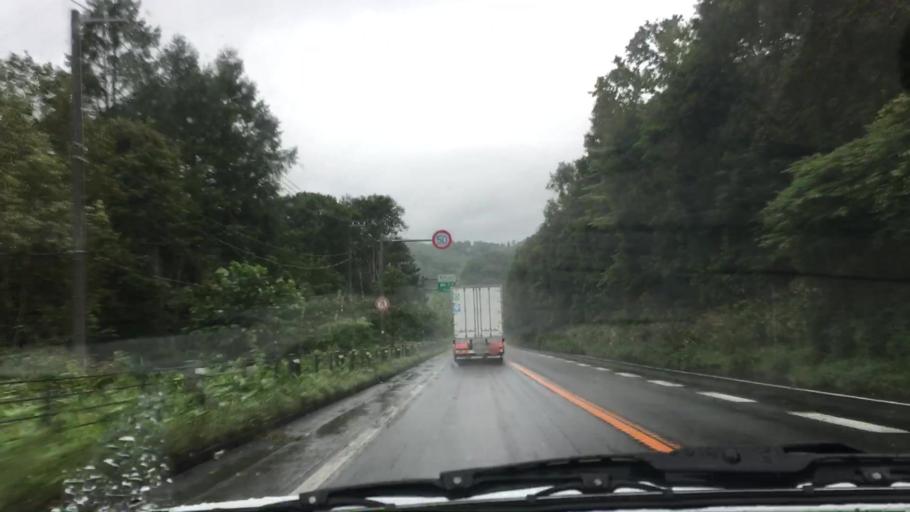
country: JP
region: Hokkaido
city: Niseko Town
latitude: 42.5985
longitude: 140.6663
